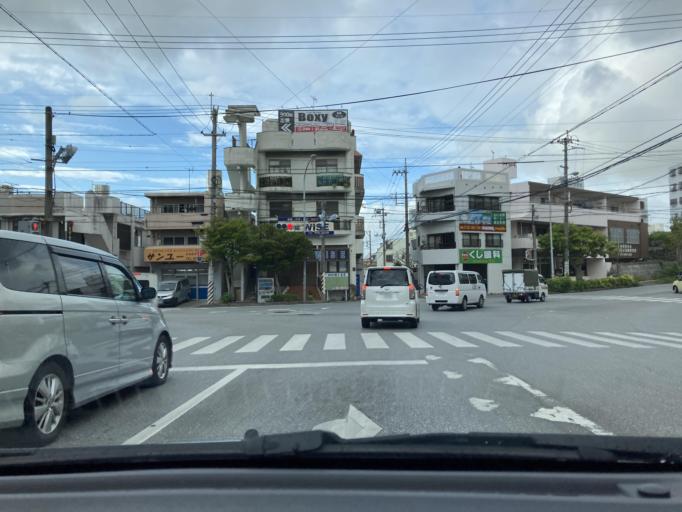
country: JP
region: Okinawa
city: Naha-shi
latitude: 26.2018
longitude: 127.6973
